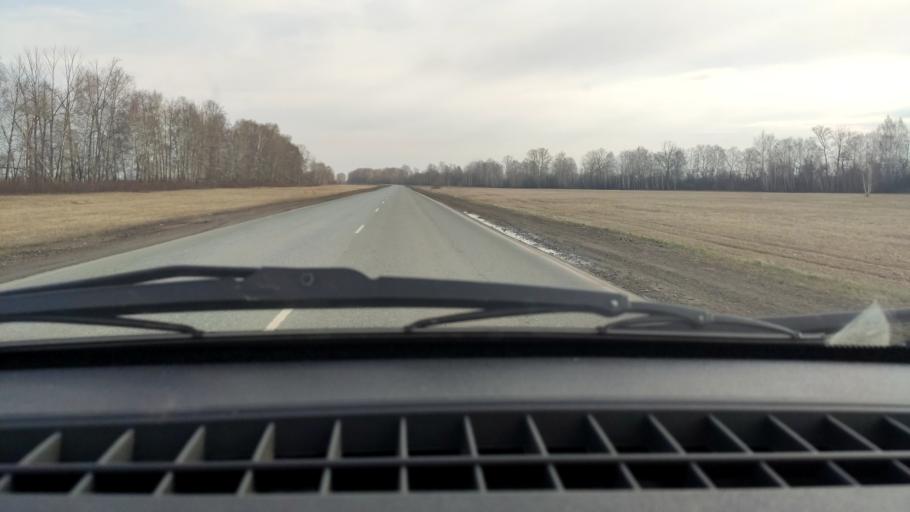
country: RU
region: Bashkortostan
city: Chishmy
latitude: 54.4050
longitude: 55.2168
